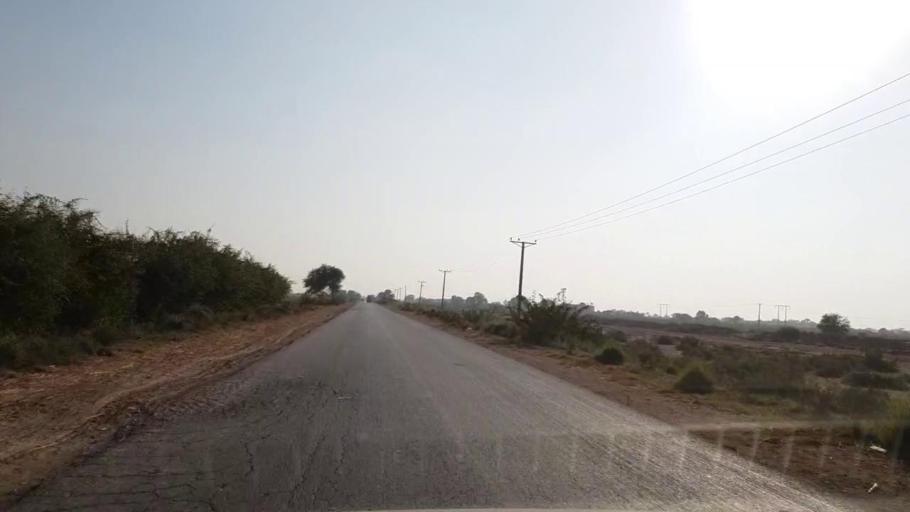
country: PK
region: Sindh
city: Bulri
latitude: 24.8948
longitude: 68.3451
